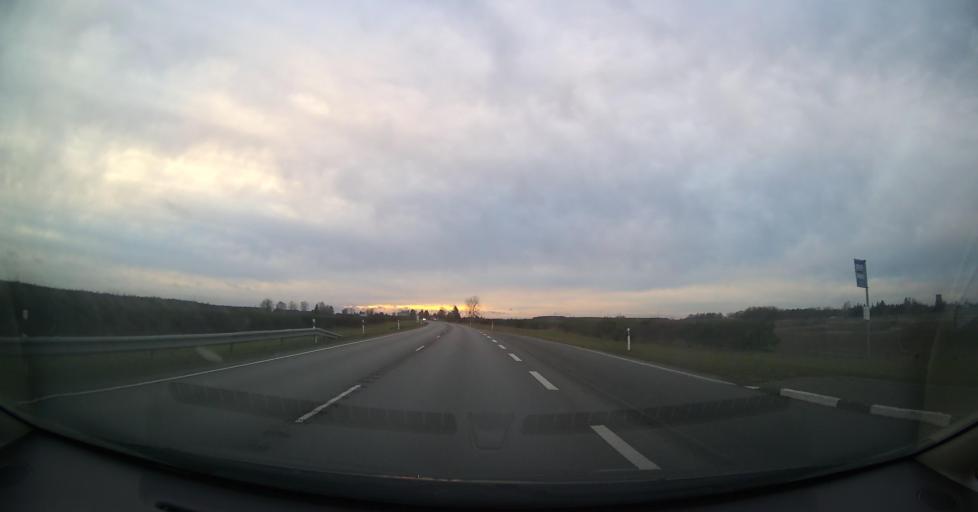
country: EE
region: Ida-Virumaa
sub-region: Kohtla-Nomme vald
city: Kohtla-Nomme
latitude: 59.4209
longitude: 27.1773
